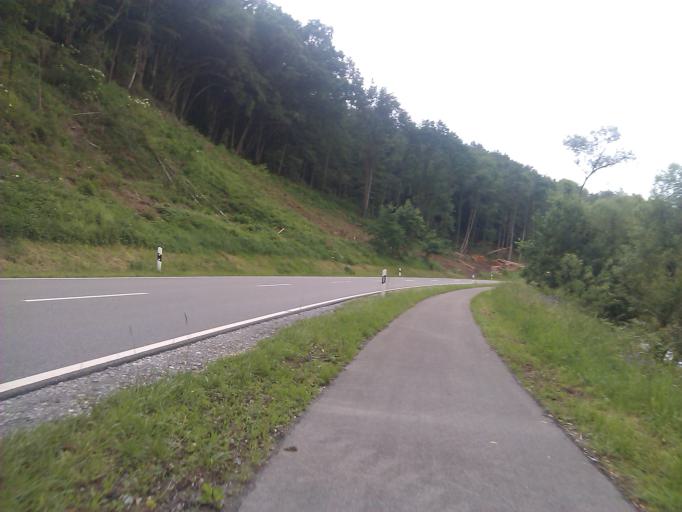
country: DE
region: Baden-Wuerttemberg
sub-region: Regierungsbezirk Stuttgart
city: Abtsgmund
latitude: 48.9087
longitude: 9.9672
